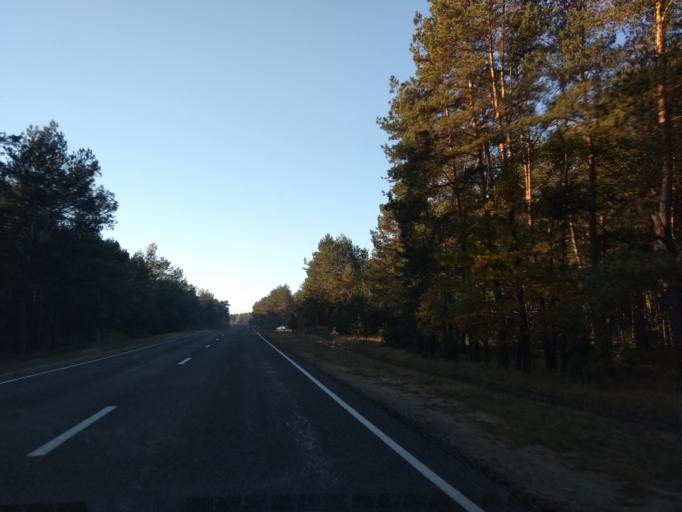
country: BY
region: Brest
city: Kobryn
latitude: 52.1037
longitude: 24.2807
